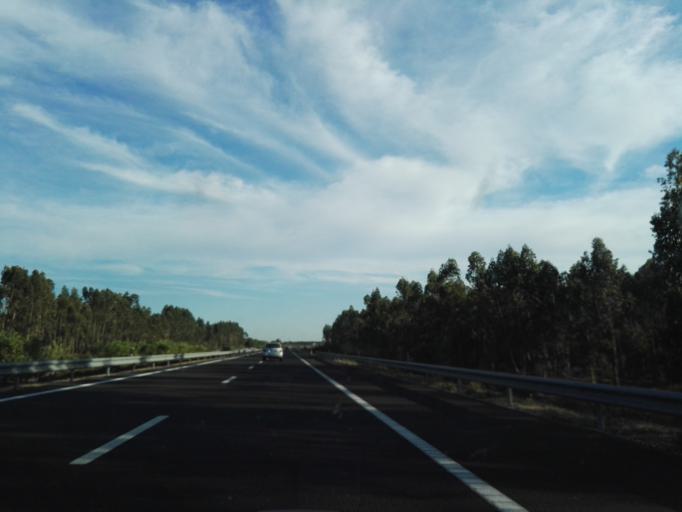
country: PT
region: Santarem
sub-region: Benavente
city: Poceirao
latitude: 38.7946
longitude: -8.6930
